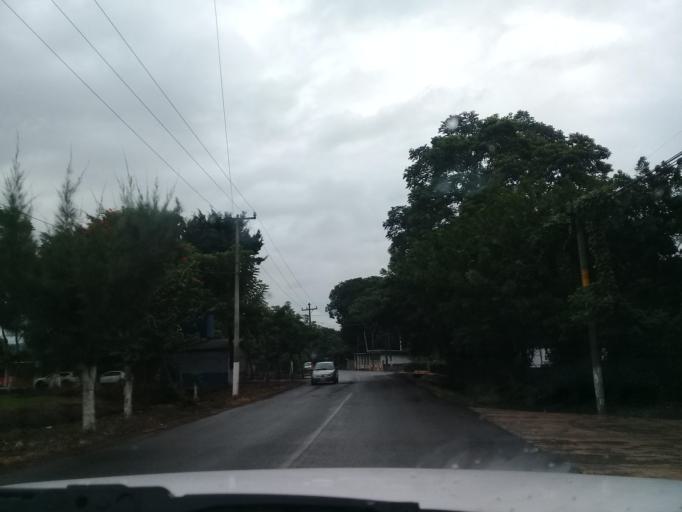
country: MX
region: Veracruz
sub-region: San Andres Tuxtla
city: Cerro las Iguanas
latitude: 18.4241
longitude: -95.2174
